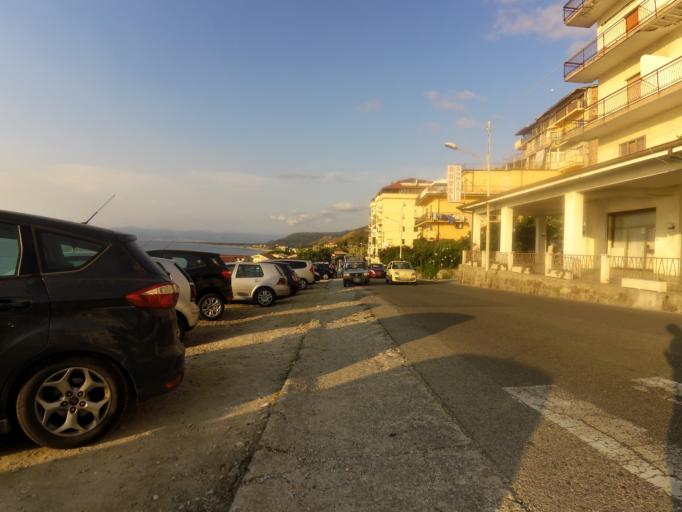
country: IT
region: Calabria
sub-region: Provincia di Vibo-Valentia
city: Pizzo
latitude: 38.7416
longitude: 16.1752
